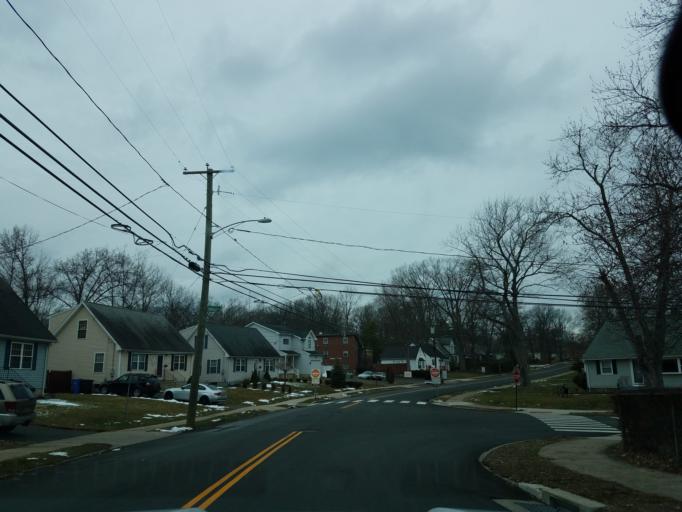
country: US
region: Connecticut
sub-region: Hartford County
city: New Britain
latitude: 41.6936
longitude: -72.7971
